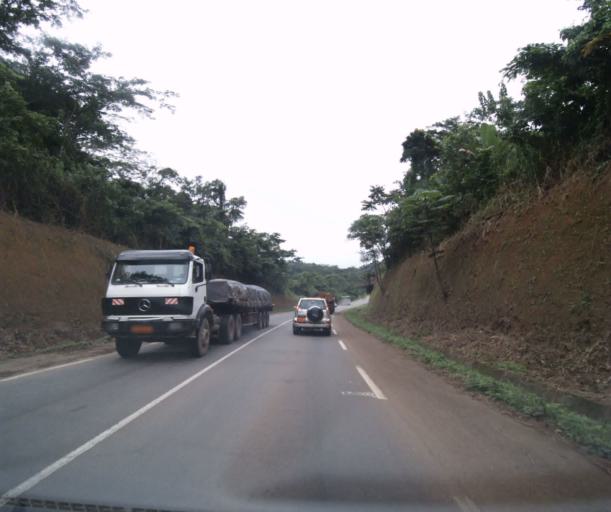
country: CM
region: Centre
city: Mbankomo
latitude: 3.7651
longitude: 11.1309
